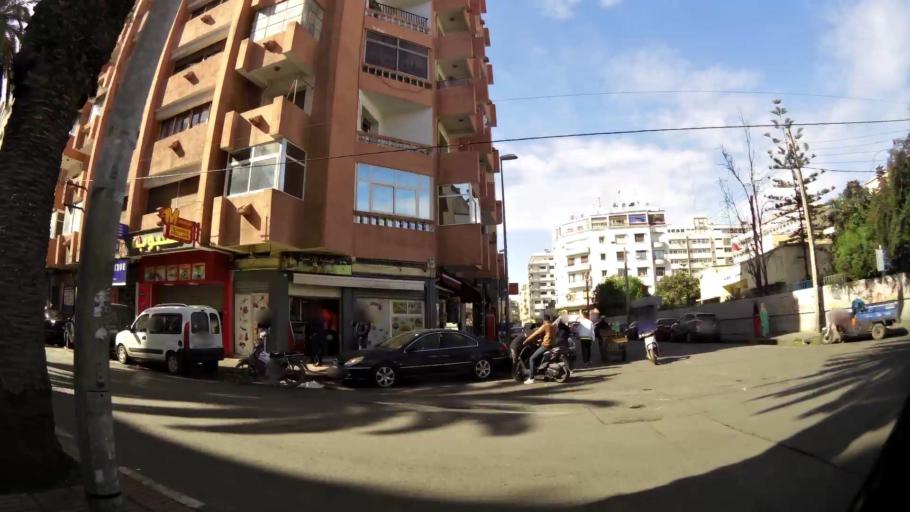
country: MA
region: Grand Casablanca
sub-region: Casablanca
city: Casablanca
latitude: 33.5923
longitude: -7.5925
